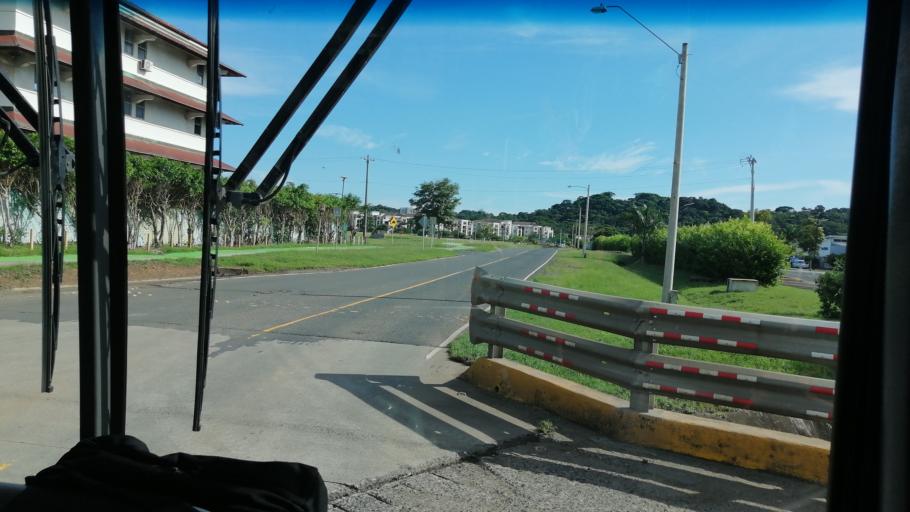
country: PA
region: Panama
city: Veracruz
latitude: 8.9112
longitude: -79.5920
